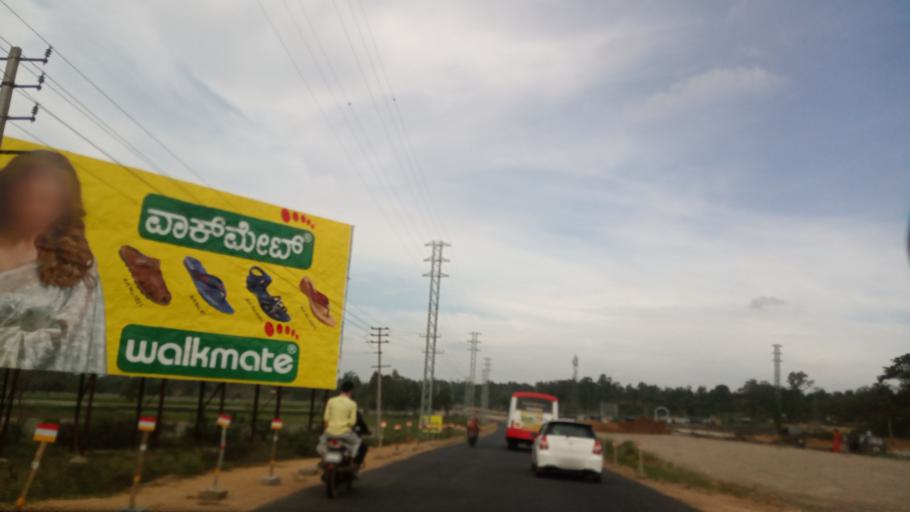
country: IN
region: Karnataka
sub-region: Mandya
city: Shrirangapattana
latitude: 12.4444
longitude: 76.7317
